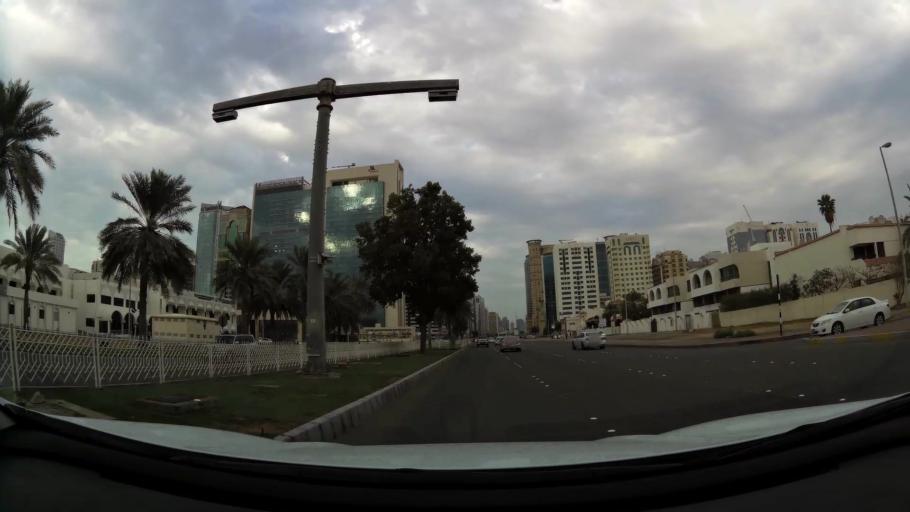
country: AE
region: Abu Dhabi
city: Abu Dhabi
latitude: 24.4682
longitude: 54.3684
